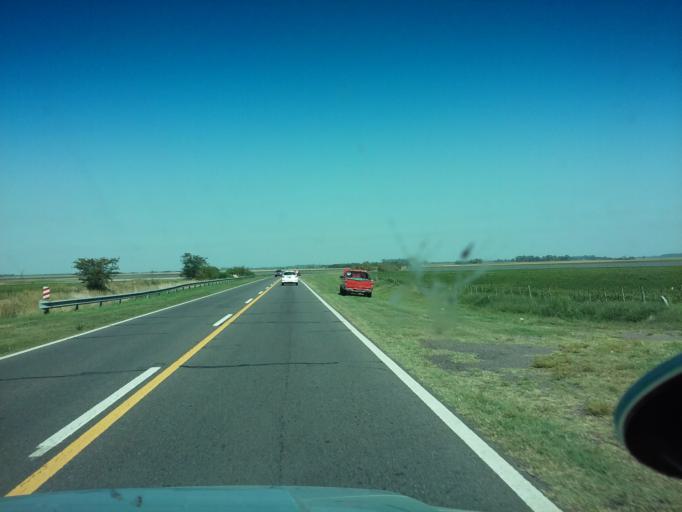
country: AR
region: Buenos Aires
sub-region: Partido de Alberti
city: Alberti
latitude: -35.0606
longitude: -60.2827
